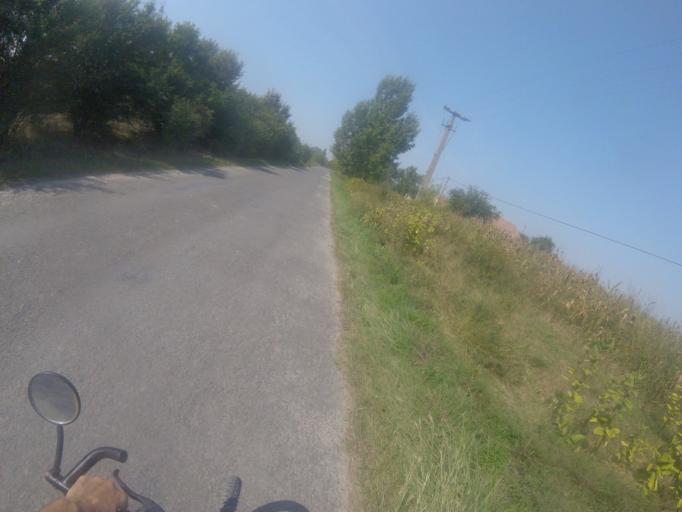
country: HU
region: Bacs-Kiskun
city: Ersekcsanad
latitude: 46.2571
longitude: 18.9283
